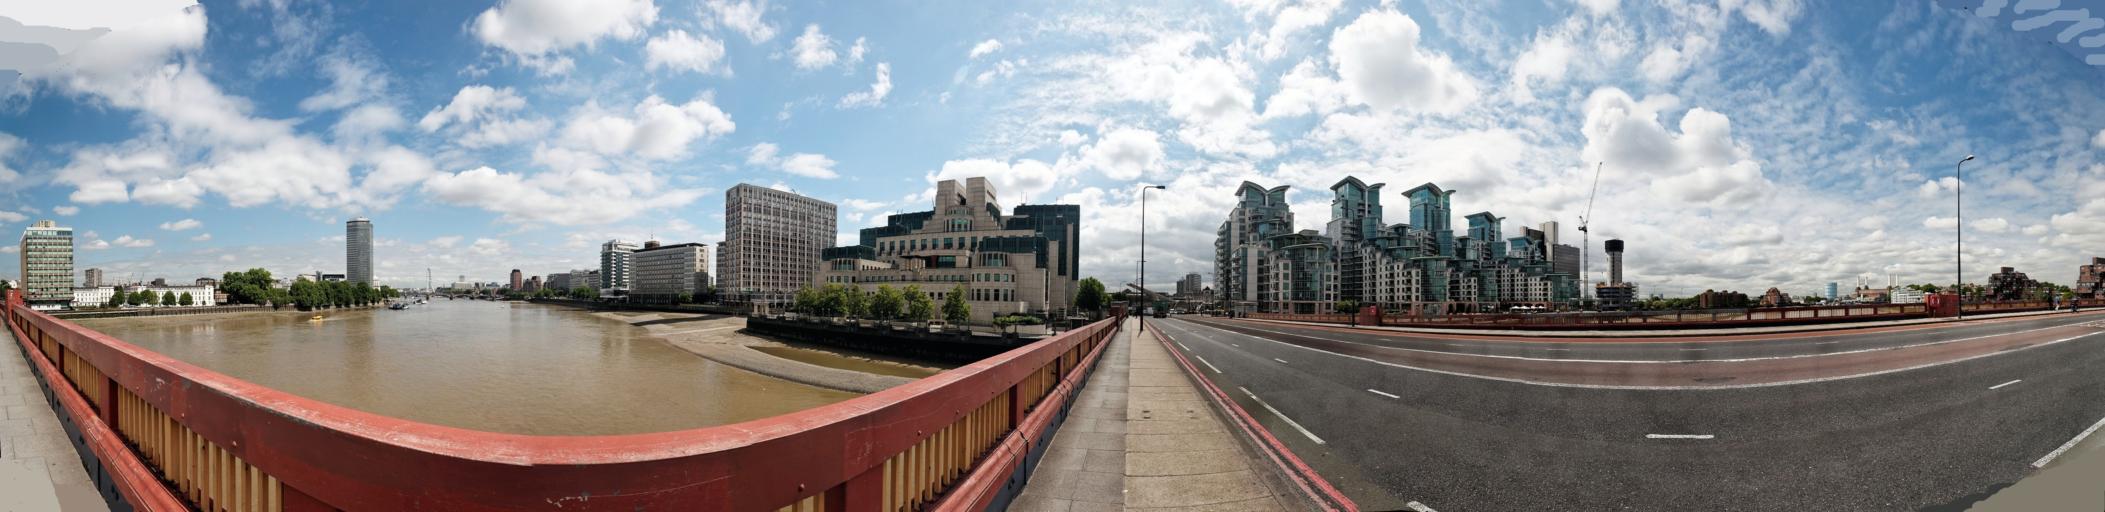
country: GB
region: England
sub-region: Greater London
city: City of Westminster
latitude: 51.4875
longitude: -0.1265
